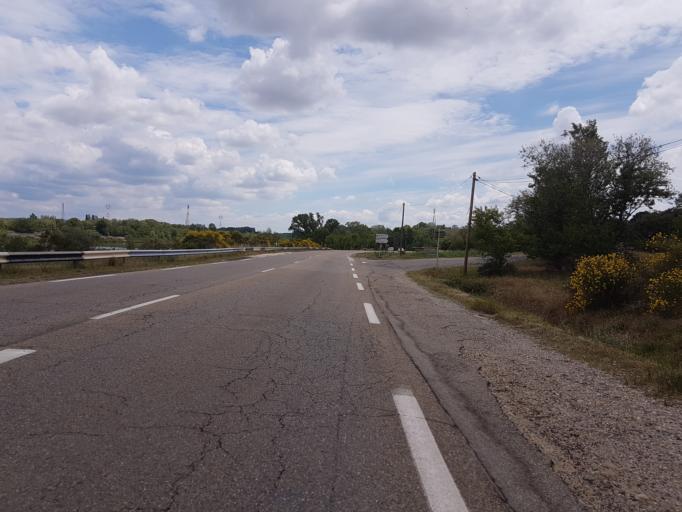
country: FR
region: Languedoc-Roussillon
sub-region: Departement du Gard
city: Vallabregues
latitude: 43.8407
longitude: 4.6200
